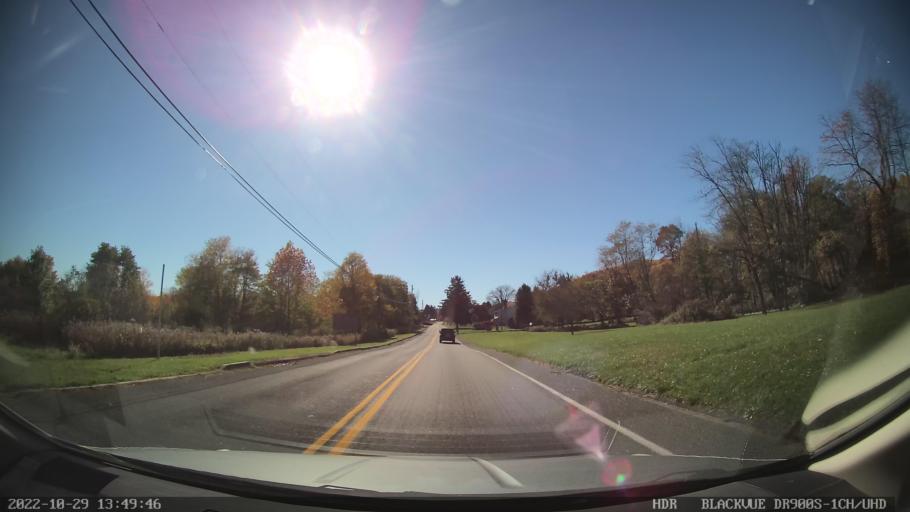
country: US
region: Pennsylvania
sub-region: Lehigh County
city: Emmaus
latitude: 40.5397
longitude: -75.4550
